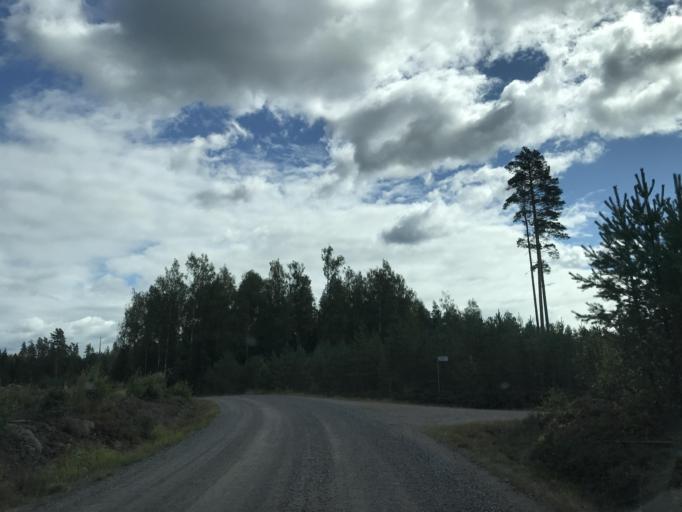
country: FI
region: Uusimaa
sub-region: Helsinki
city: Kaerkoelae
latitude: 60.6352
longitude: 23.7911
